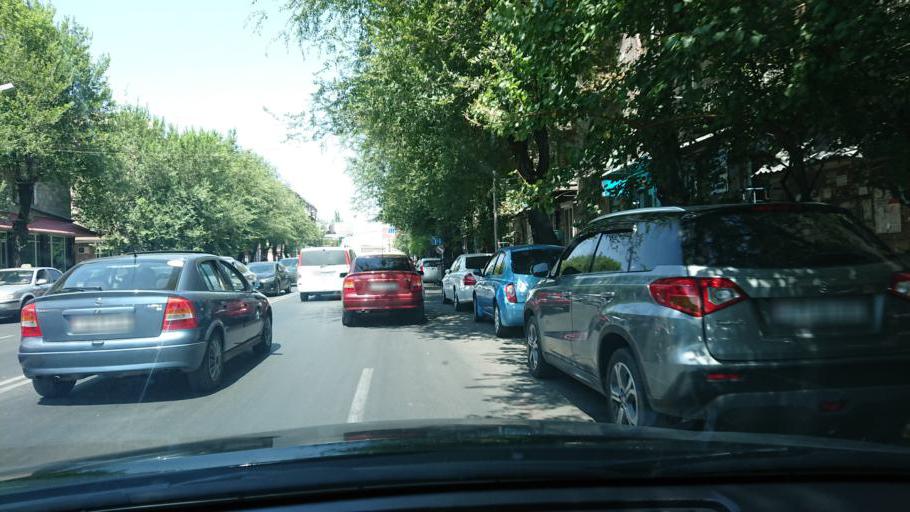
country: AM
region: Yerevan
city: Yerevan
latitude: 40.2040
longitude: 44.4979
